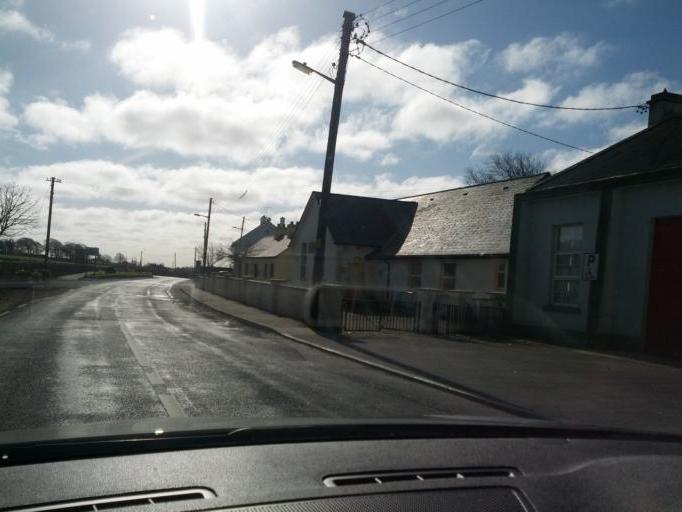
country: IE
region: Connaught
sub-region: County Galway
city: Ballinasloe
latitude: 53.3965
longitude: -8.3318
